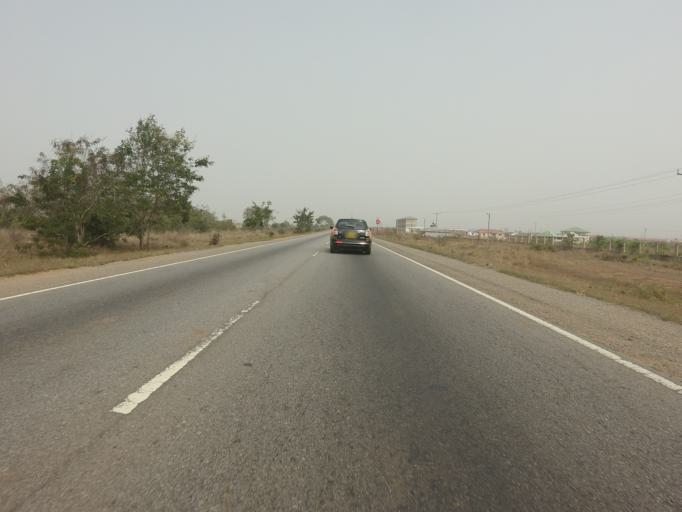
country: GH
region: Greater Accra
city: Tema
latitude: 5.8569
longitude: 0.2687
